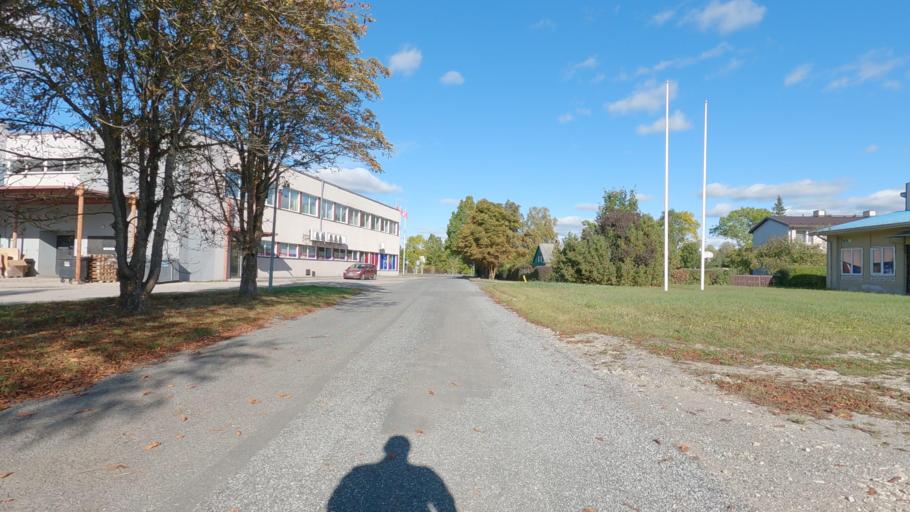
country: EE
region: Raplamaa
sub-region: Rapla vald
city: Rapla
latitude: 58.9958
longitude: 24.8104
